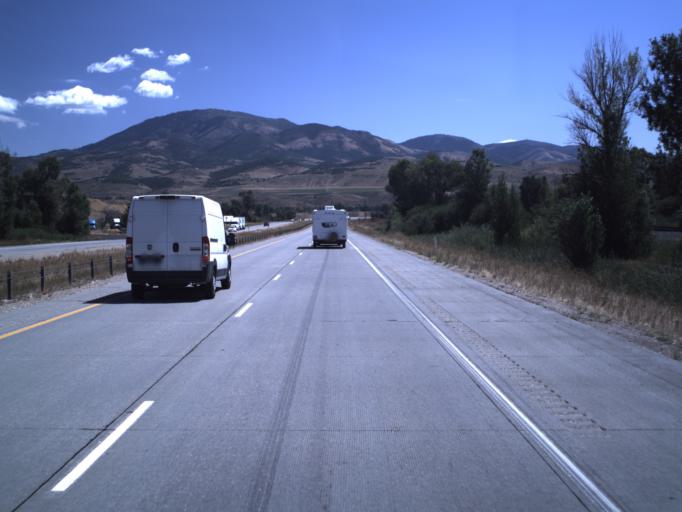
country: US
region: Utah
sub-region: Morgan County
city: Mountain Green
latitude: 41.1377
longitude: -111.8010
